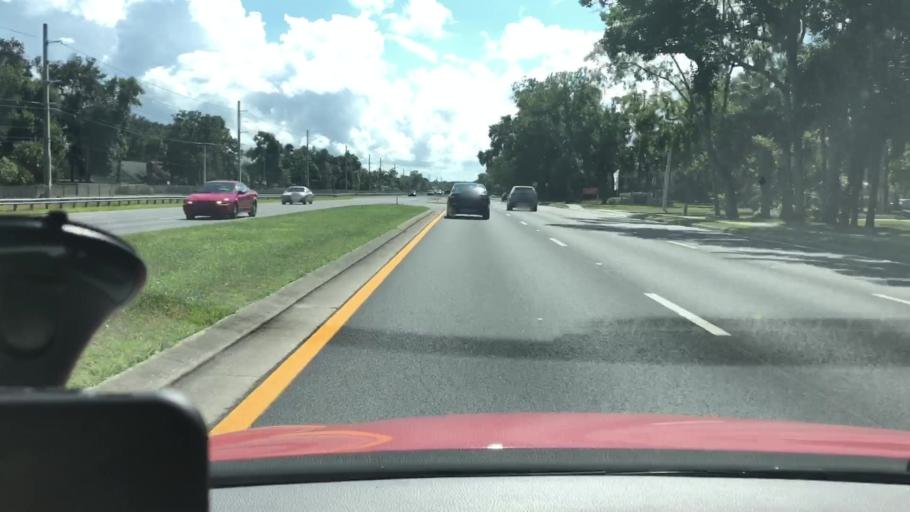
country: US
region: Florida
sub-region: Volusia County
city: Daytona Beach
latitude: 29.1852
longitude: -81.0303
